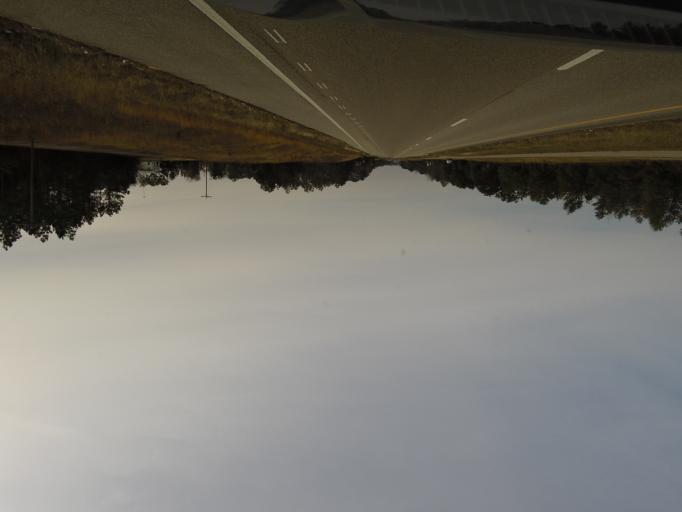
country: US
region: Alabama
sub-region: Houston County
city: Ashford
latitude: 31.1309
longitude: -85.0838
